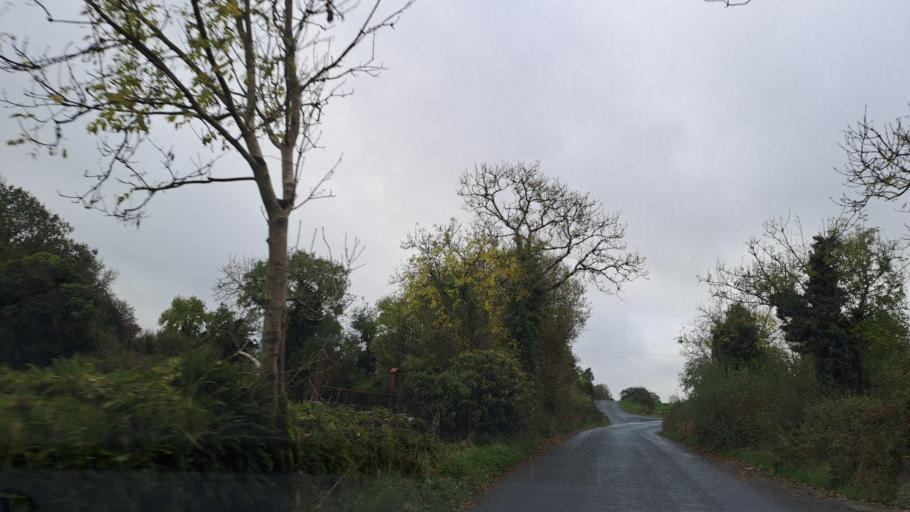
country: IE
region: Ulster
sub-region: An Cabhan
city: Bailieborough
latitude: 53.9947
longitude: -6.9743
